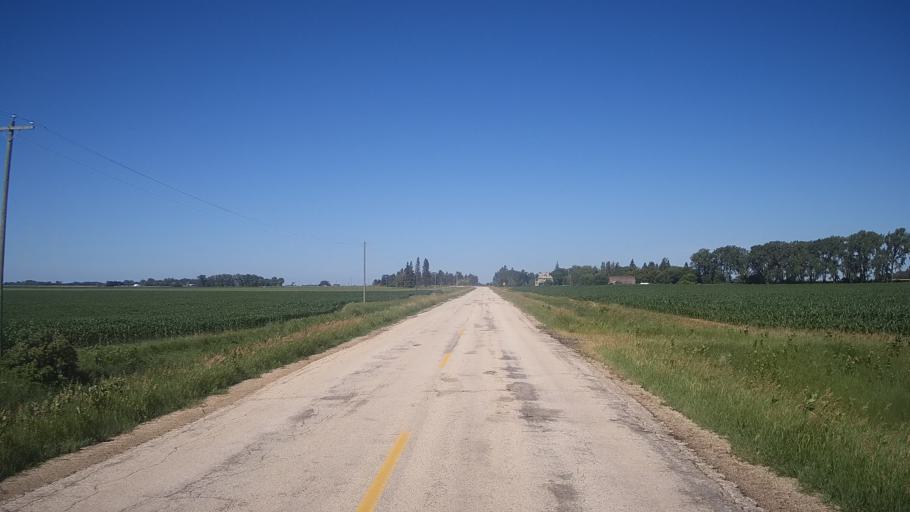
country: CA
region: Manitoba
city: Portage la Prairie
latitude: 50.0437
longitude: -98.0490
